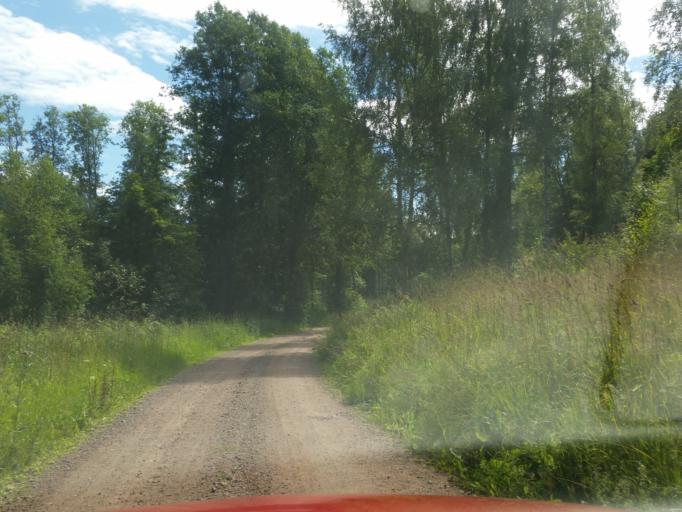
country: SE
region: Dalarna
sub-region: Gagnefs Kommun
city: Gagnef
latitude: 60.6567
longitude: 15.1378
